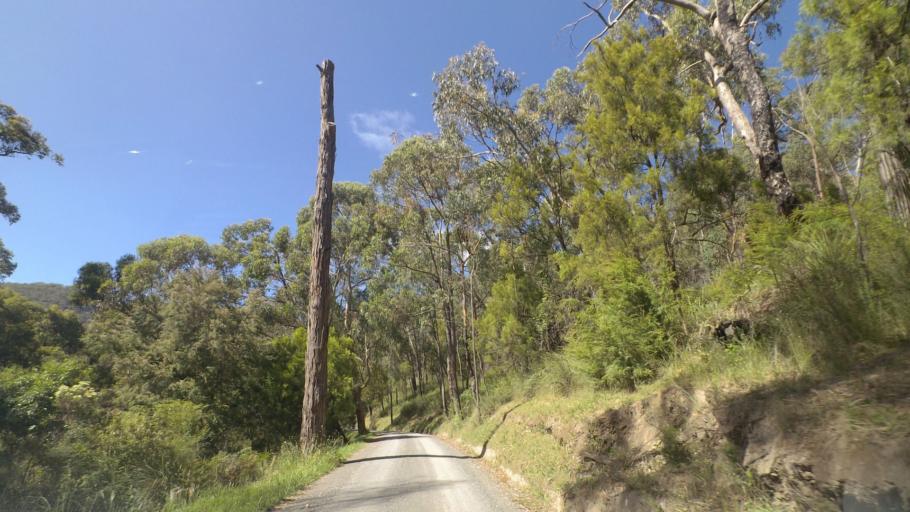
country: AU
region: Victoria
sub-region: Yarra Ranges
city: Kalorama
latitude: -37.8050
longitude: 145.3667
